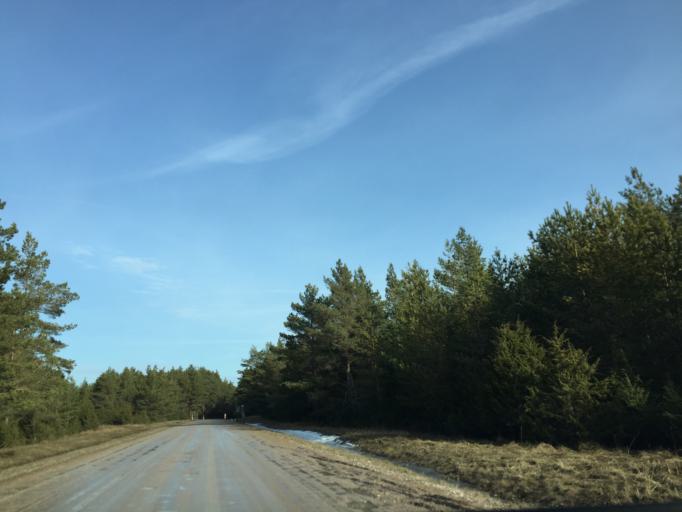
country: EE
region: Saare
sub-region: Kuressaare linn
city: Kuressaare
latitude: 58.2780
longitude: 21.9160
